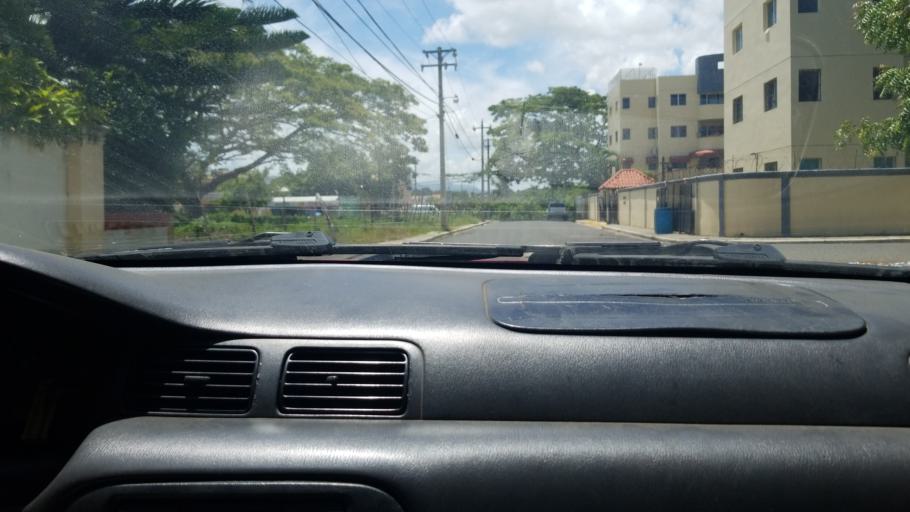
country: DO
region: Santiago
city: Santiago de los Caballeros
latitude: 19.4854
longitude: -70.6878
